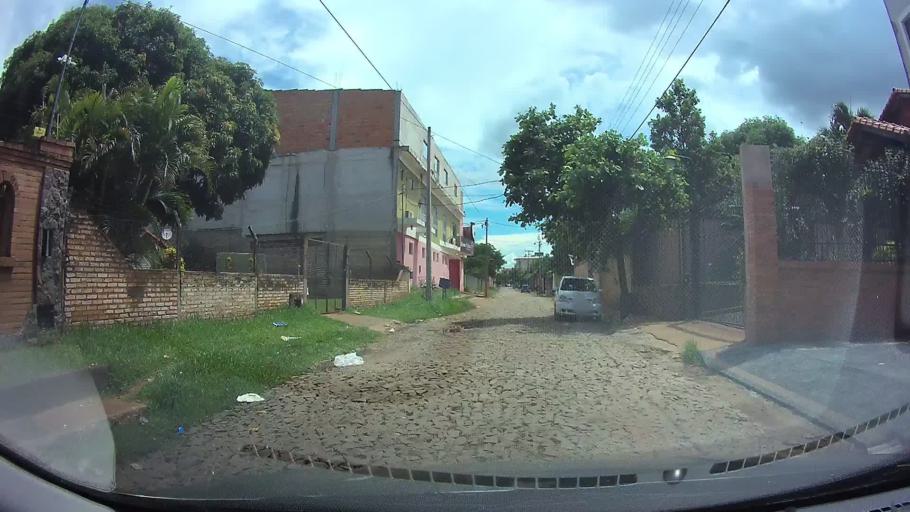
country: PY
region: Central
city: Fernando de la Mora
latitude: -25.3144
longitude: -57.5243
